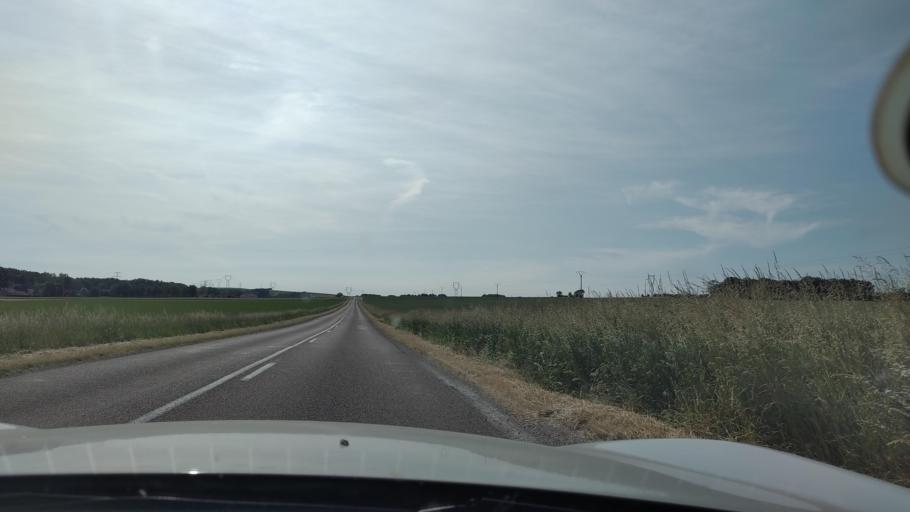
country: FR
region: Champagne-Ardenne
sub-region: Departement de l'Aube
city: Nogent-sur-Seine
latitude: 48.4650
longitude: 3.5757
